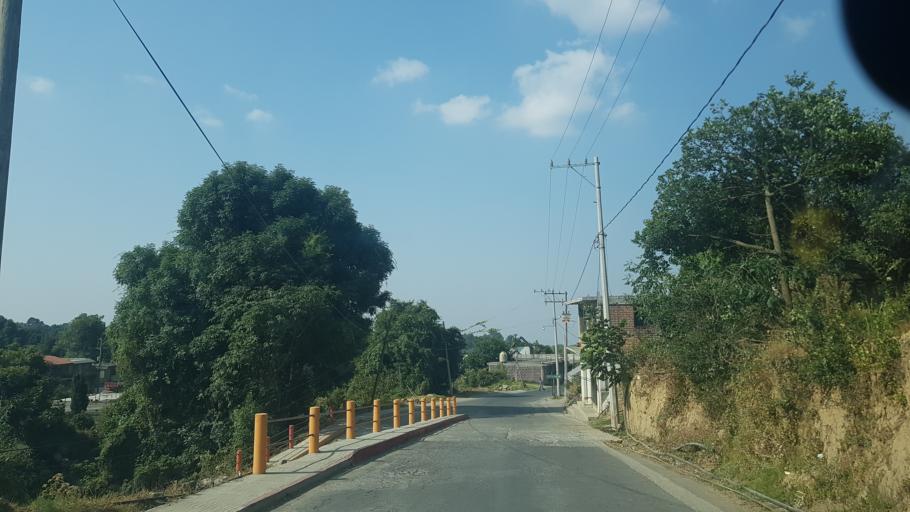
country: MX
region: Morelos
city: Hueyapan
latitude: 18.8925
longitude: -98.6777
